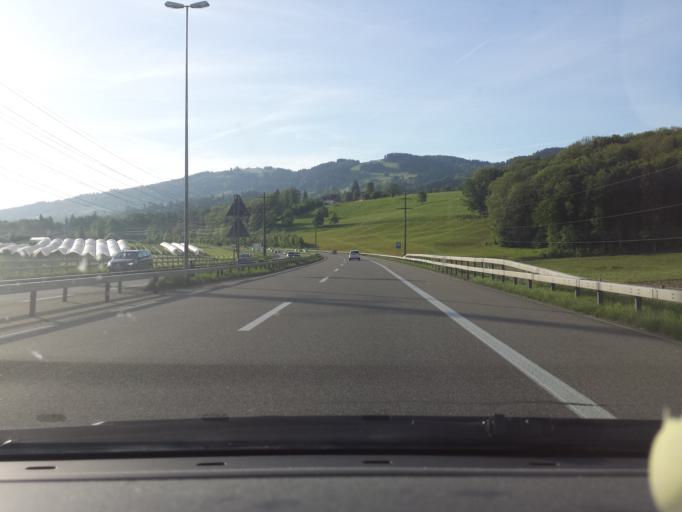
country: CH
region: Saint Gallen
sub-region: Wahlkreis Rorschach
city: Goldach
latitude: 47.4679
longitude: 9.4574
